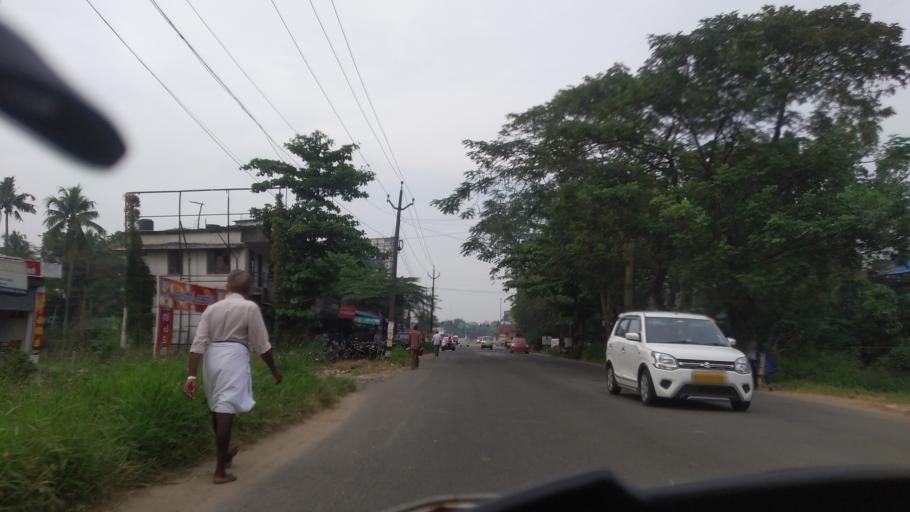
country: IN
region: Kerala
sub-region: Ernakulam
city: Elur
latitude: 10.0595
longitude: 76.2898
